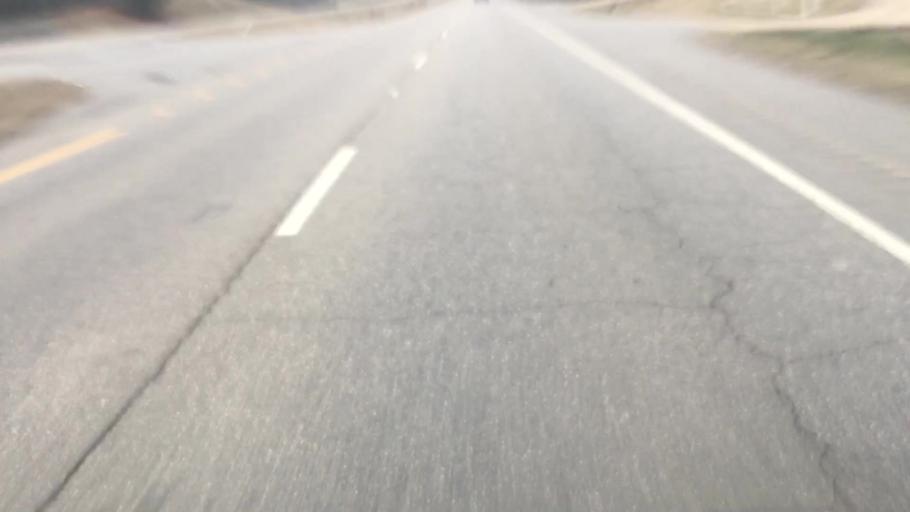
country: US
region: Alabama
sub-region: Walker County
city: Sumiton
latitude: 33.7402
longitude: -87.0338
